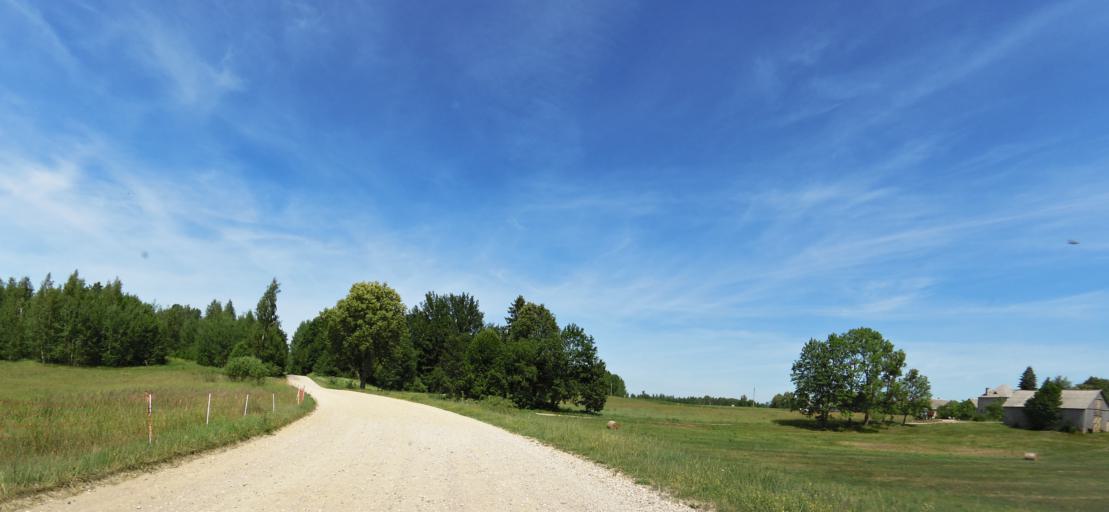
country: LT
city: Sirvintos
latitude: 55.1218
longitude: 24.8552
